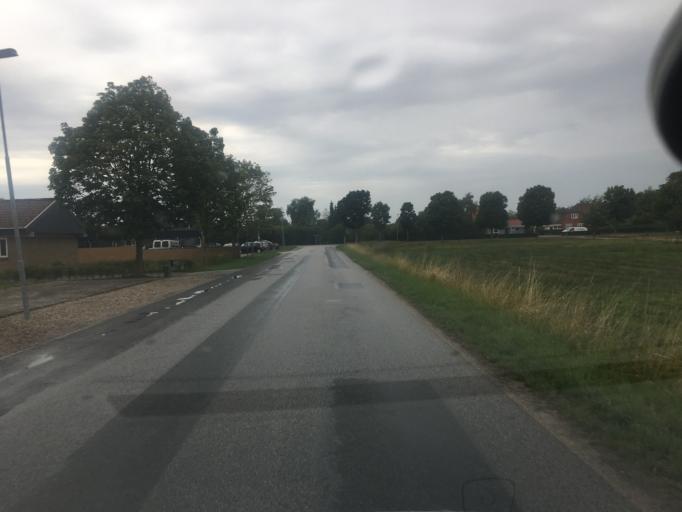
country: DK
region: South Denmark
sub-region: Tonder Kommune
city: Logumkloster
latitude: 55.0504
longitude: 8.9460
